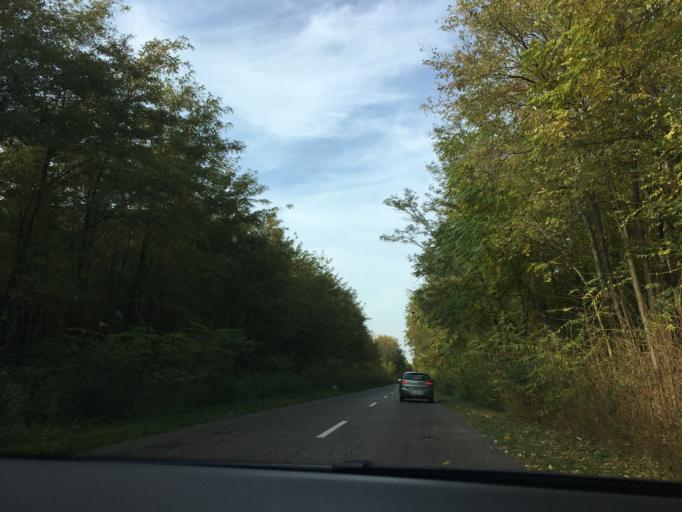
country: HU
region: Szabolcs-Szatmar-Bereg
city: Mariapocs
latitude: 47.8563
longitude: 22.0330
